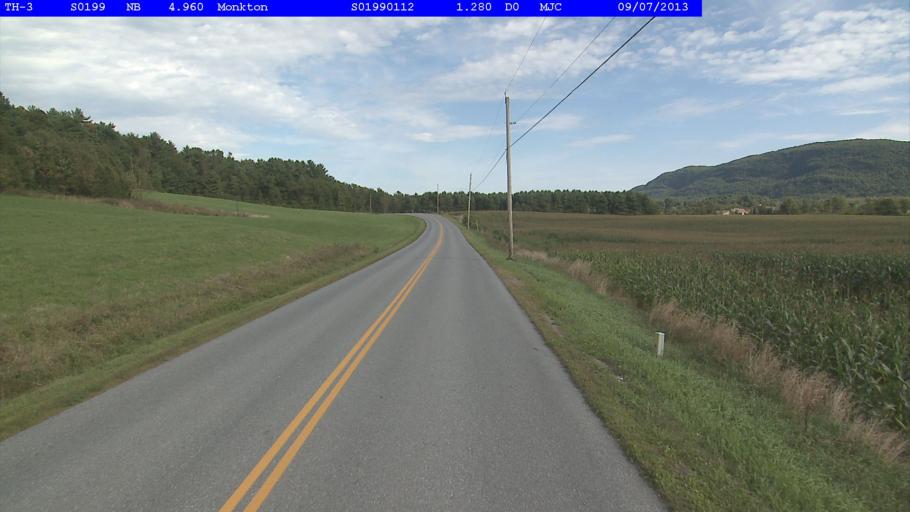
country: US
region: Vermont
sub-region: Addison County
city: Bristol
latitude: 44.1990
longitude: -73.1101
